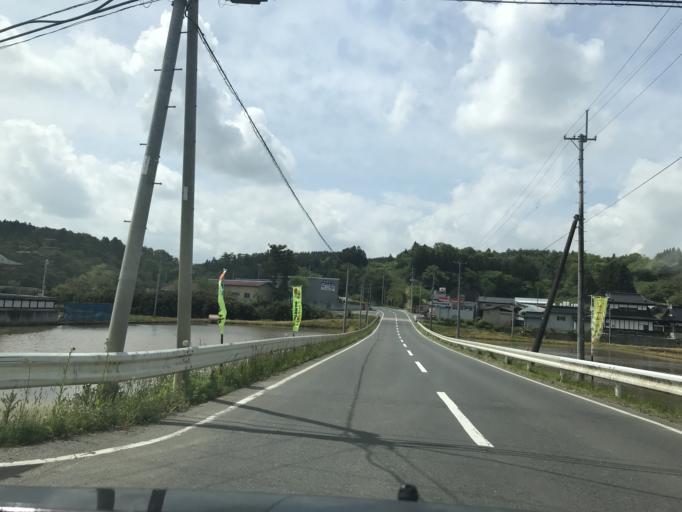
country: JP
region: Iwate
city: Ichinoseki
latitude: 38.7888
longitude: 141.0014
